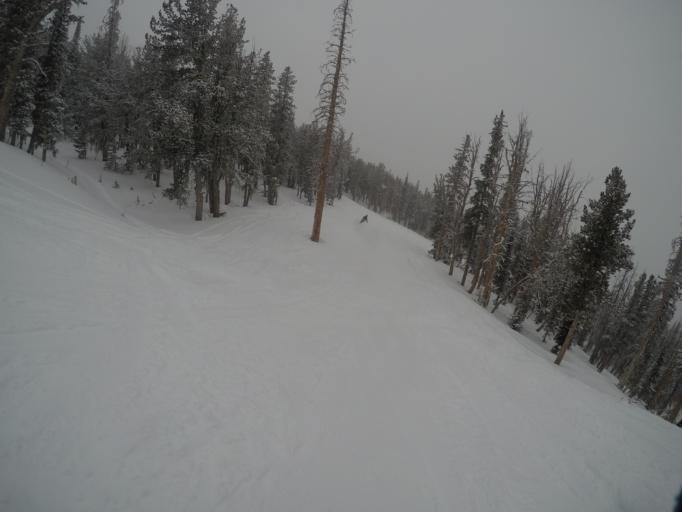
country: US
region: Montana
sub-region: Carbon County
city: Red Lodge
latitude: 45.1841
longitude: -109.3625
